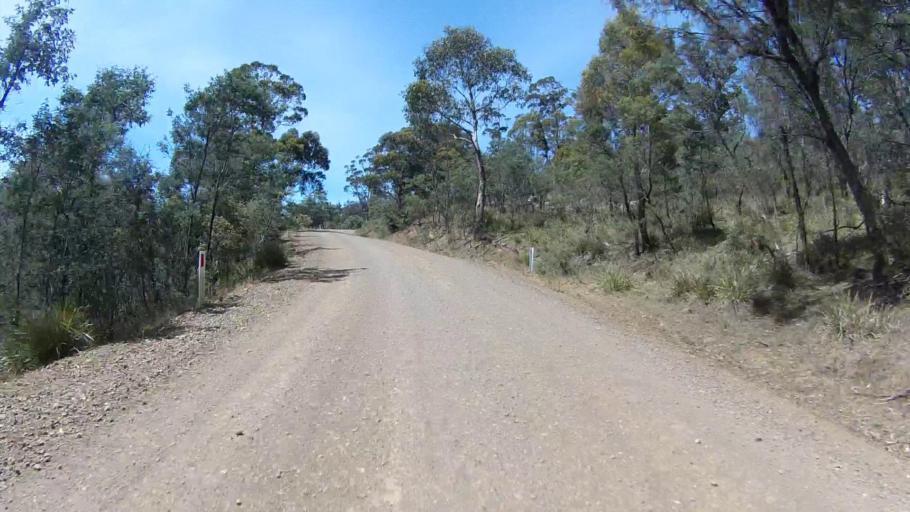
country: AU
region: Tasmania
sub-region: Sorell
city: Sorell
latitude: -42.6484
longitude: 147.7432
